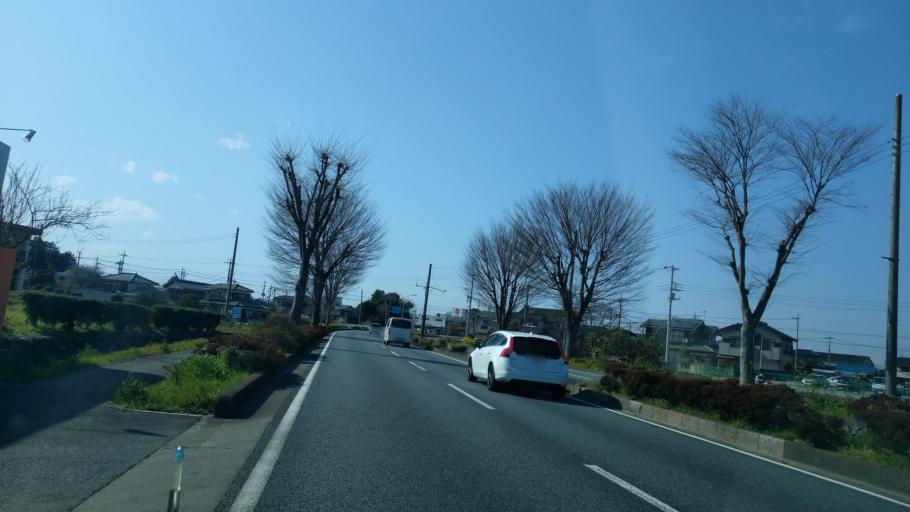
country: JP
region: Saitama
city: Sakado
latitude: 36.0096
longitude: 139.4388
